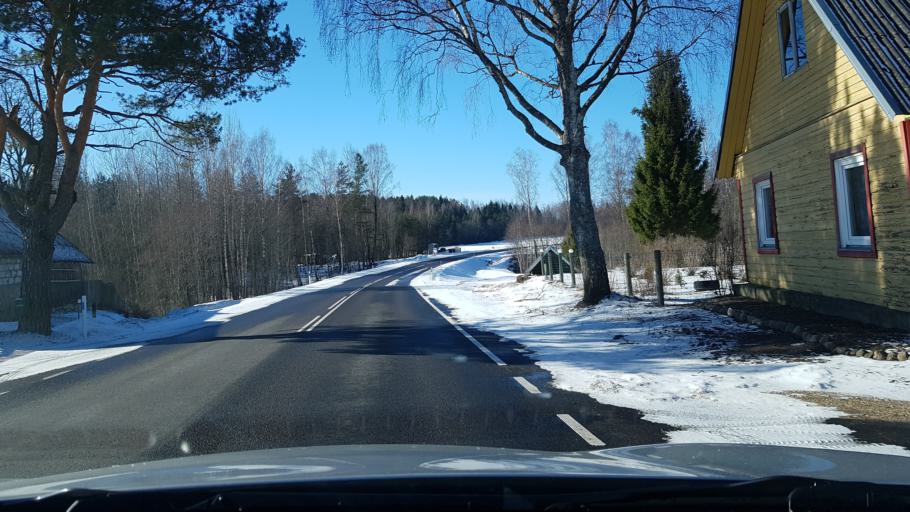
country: EE
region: Polvamaa
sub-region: Polva linn
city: Polva
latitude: 58.0923
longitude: 27.1428
